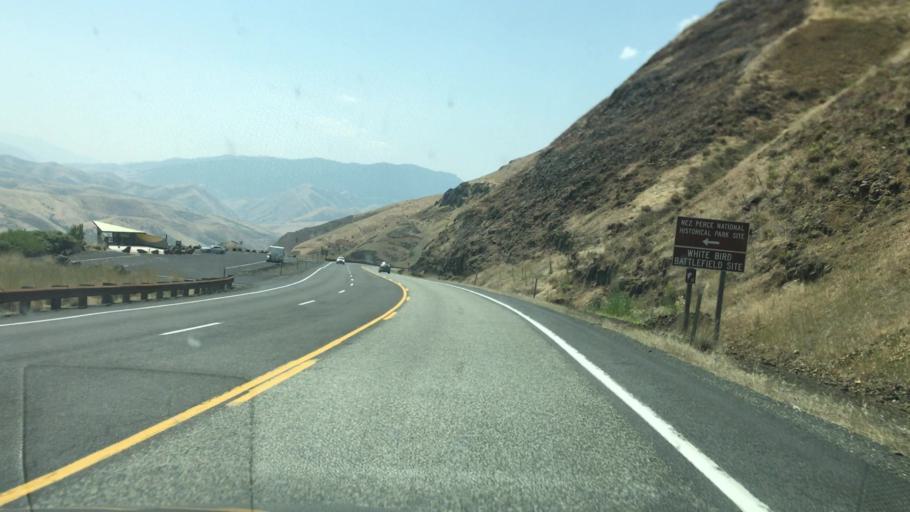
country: US
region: Idaho
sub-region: Idaho County
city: Grangeville
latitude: 45.8033
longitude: -116.2870
